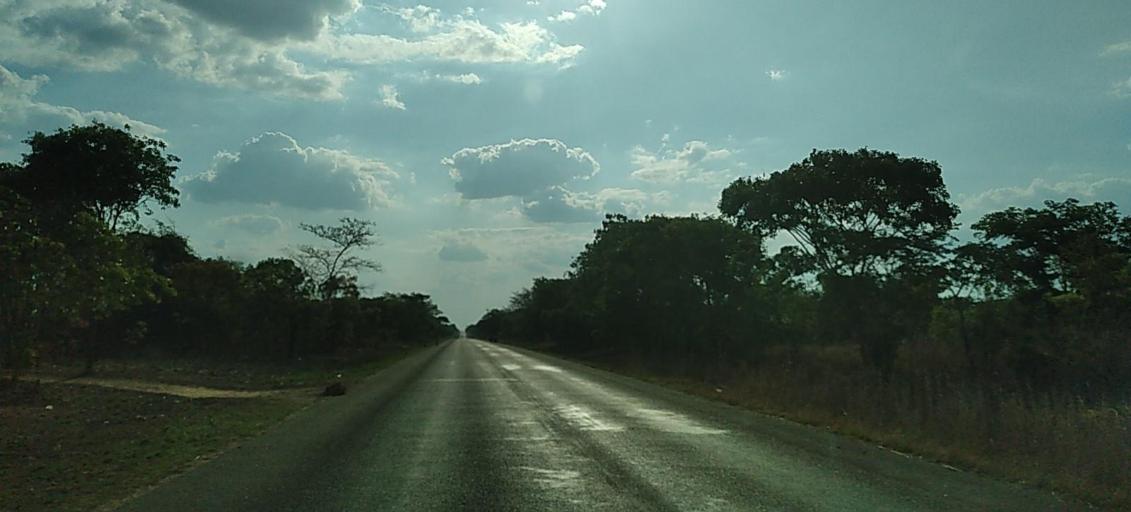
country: ZM
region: Copperbelt
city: Mpongwe
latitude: -13.3907
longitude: 28.3729
